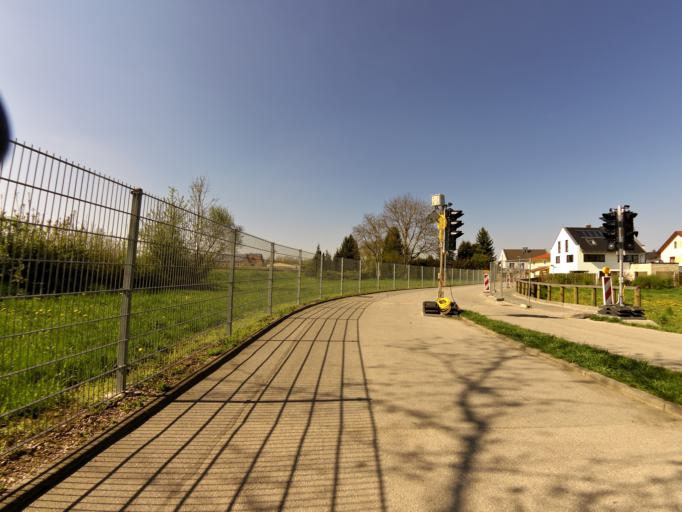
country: DE
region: Bavaria
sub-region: Lower Bavaria
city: Landshut
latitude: 48.5380
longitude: 12.1305
